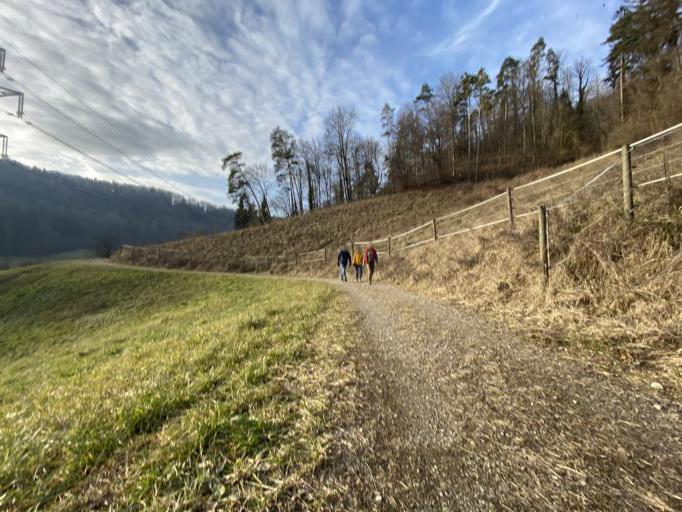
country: CH
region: Zurich
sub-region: Bezirk Winterthur
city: Toess (Kreis 4) / Vorder-Daettnau
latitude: 47.4858
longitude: 8.6925
